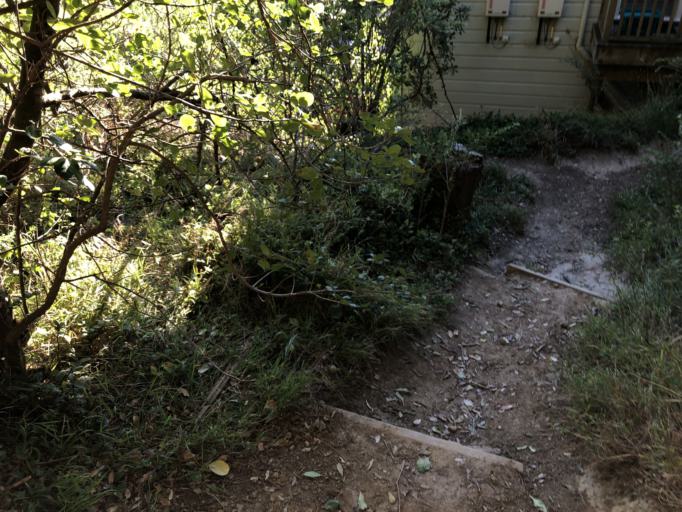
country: NZ
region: Wellington
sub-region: Wellington City
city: Wellington
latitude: -41.2992
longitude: 174.7883
